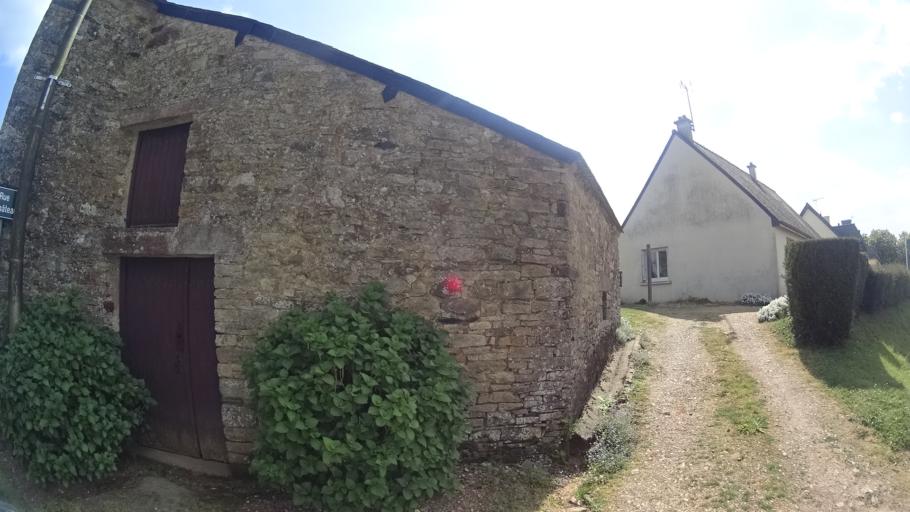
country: FR
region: Brittany
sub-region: Departement du Morbihan
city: Rieux
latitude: 47.5985
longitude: -2.1036
